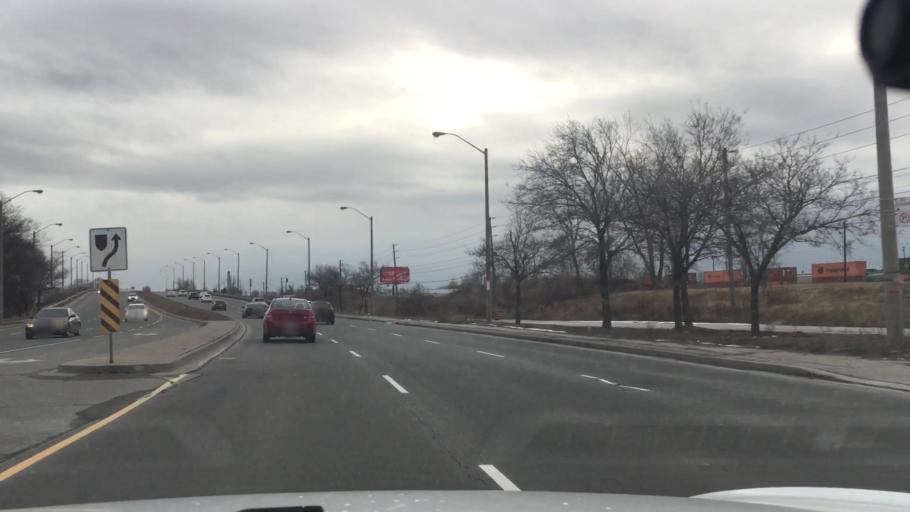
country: CA
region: Ontario
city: Scarborough
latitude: 43.8066
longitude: -79.2439
